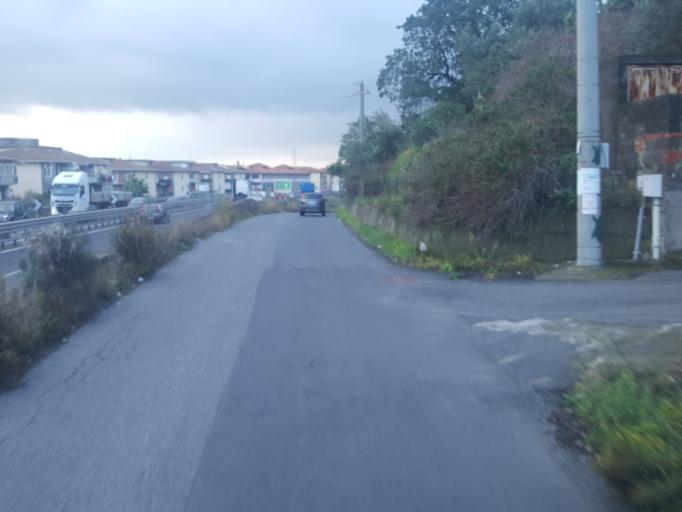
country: IT
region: Sicily
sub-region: Catania
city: Belvedere-Piano Tavola
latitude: 37.5343
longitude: 14.9851
